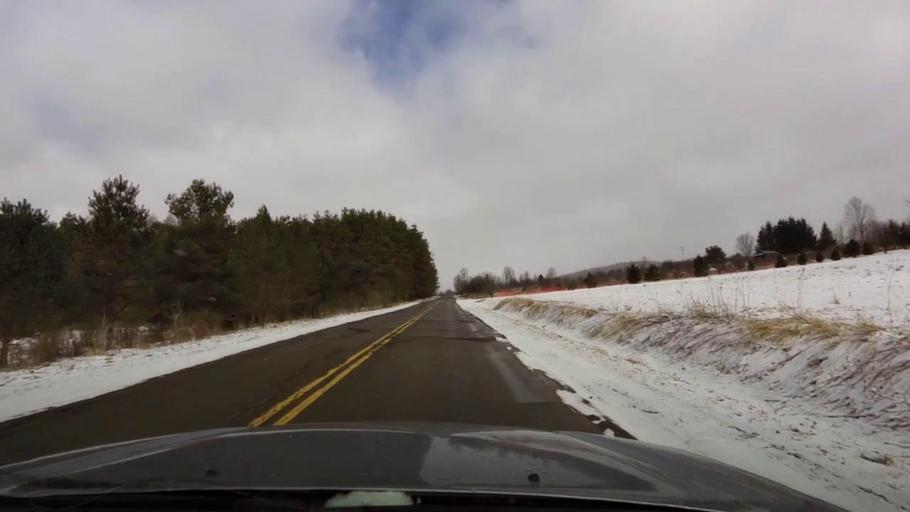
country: US
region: New York
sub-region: Cattaraugus County
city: Franklinville
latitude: 42.2987
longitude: -78.3536
